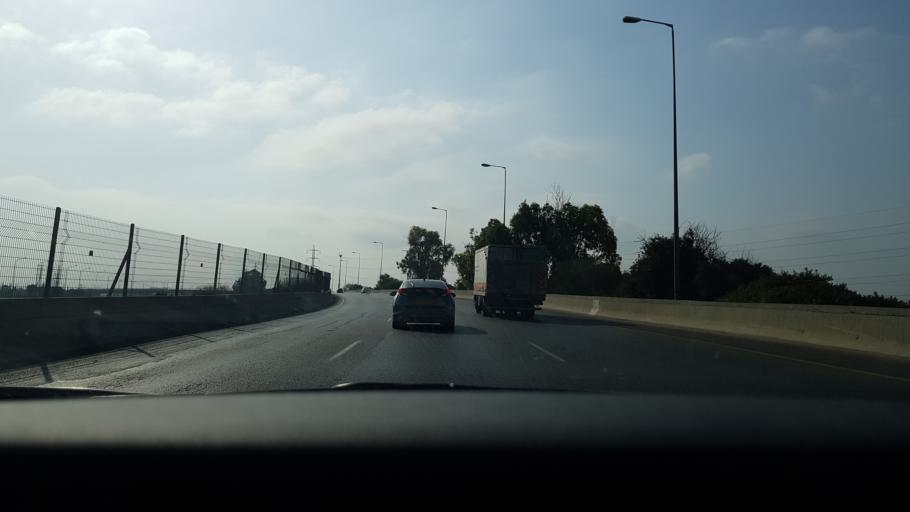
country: IL
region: Tel Aviv
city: Azor
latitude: 32.0431
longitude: 34.7881
